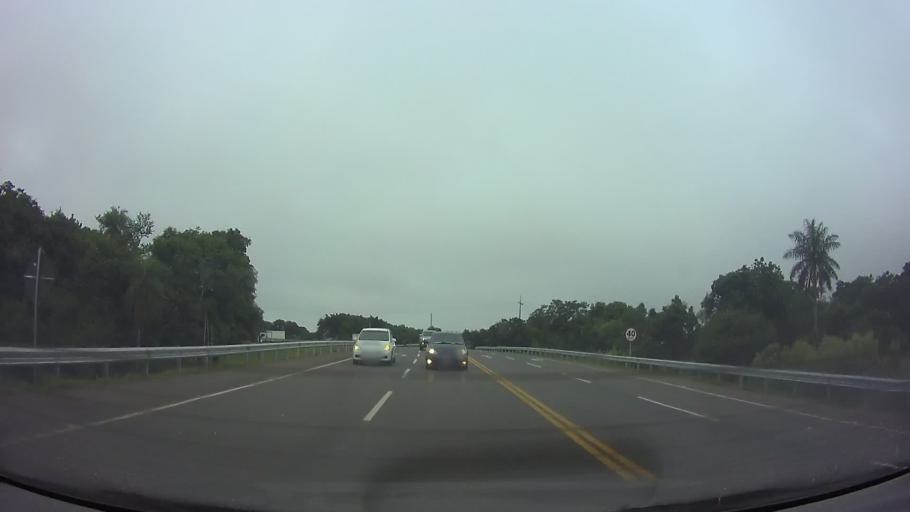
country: PY
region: Paraguari
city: Paraguari
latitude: -25.6047
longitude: -57.1869
